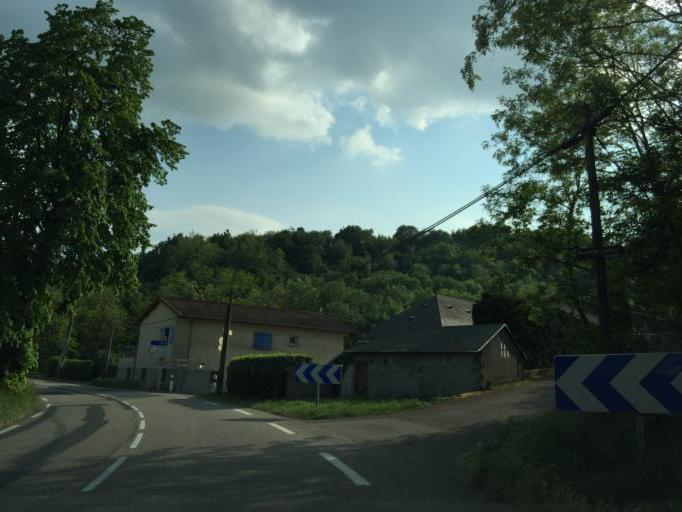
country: FR
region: Rhone-Alpes
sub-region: Departement du Rhone
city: Saint-Andeol-le-Chateau
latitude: 45.5558
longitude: 4.6816
